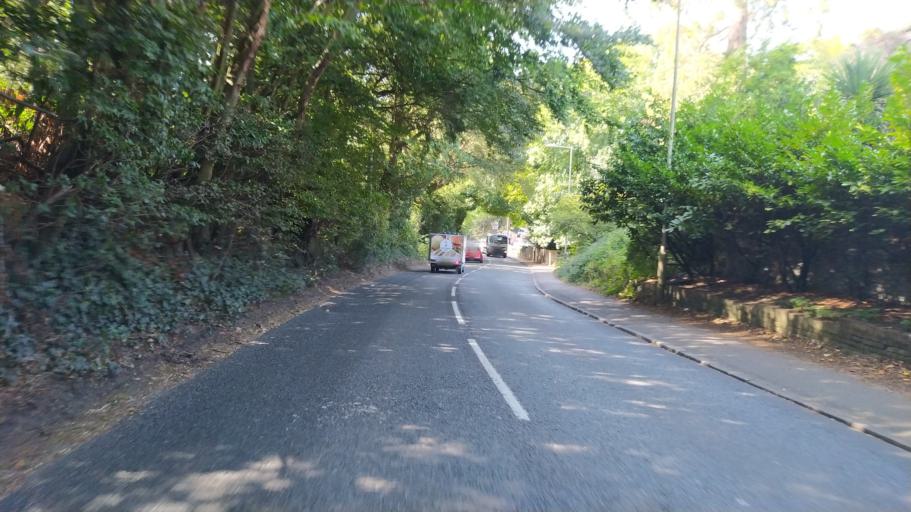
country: GB
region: England
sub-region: Hampshire
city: Botley
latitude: 50.9141
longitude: -1.2664
